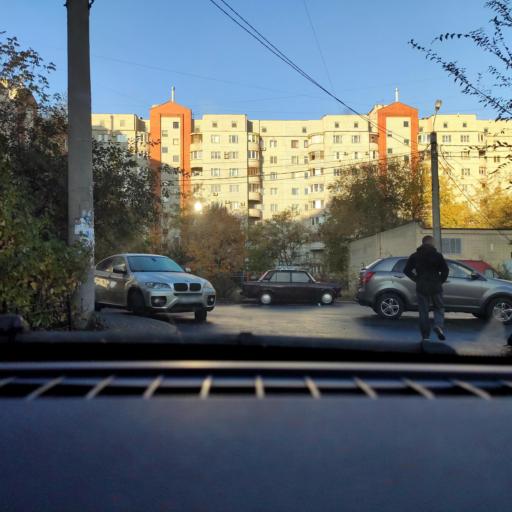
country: RU
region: Voronezj
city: Voronezh
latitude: 51.6698
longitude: 39.2880
